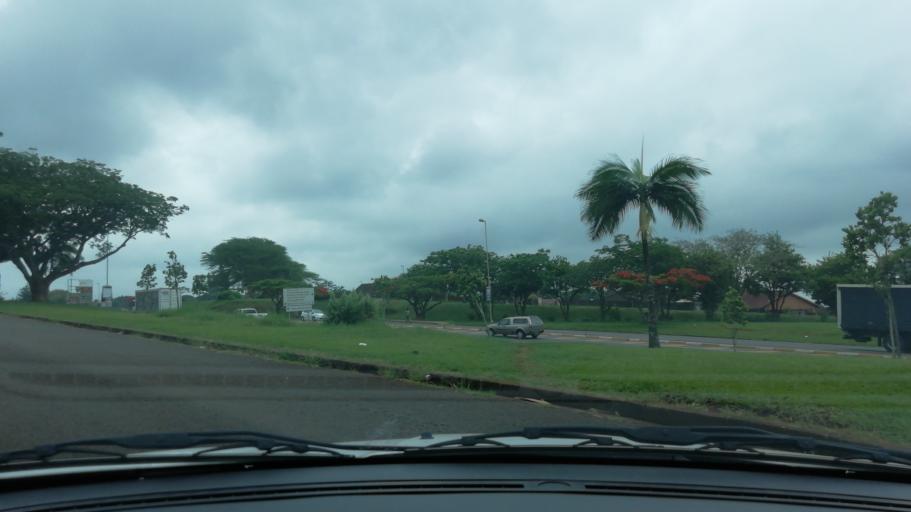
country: ZA
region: KwaZulu-Natal
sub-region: uThungulu District Municipality
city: Empangeni
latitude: -28.7606
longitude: 31.9031
